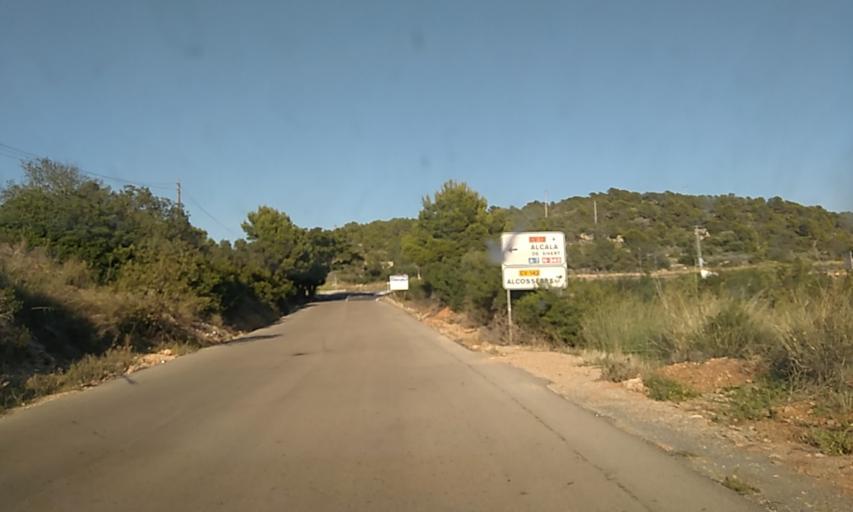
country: ES
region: Valencia
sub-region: Provincia de Castello
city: Alcoceber
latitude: 40.2495
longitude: 0.2464
